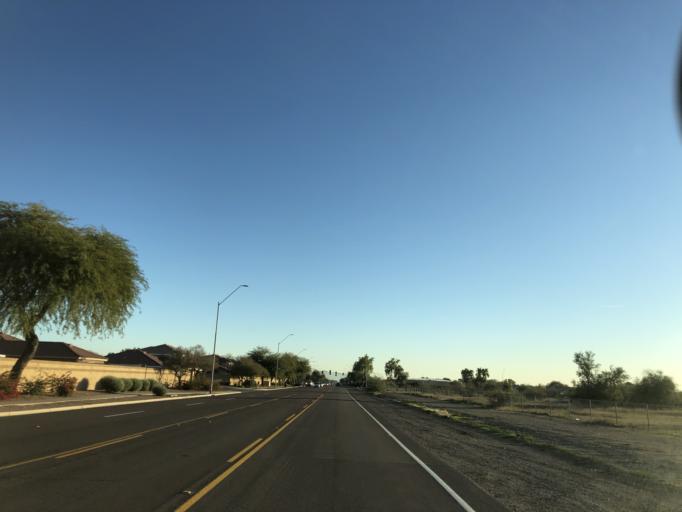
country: US
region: Arizona
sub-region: Maricopa County
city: Sun City West
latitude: 33.6917
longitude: -112.2898
